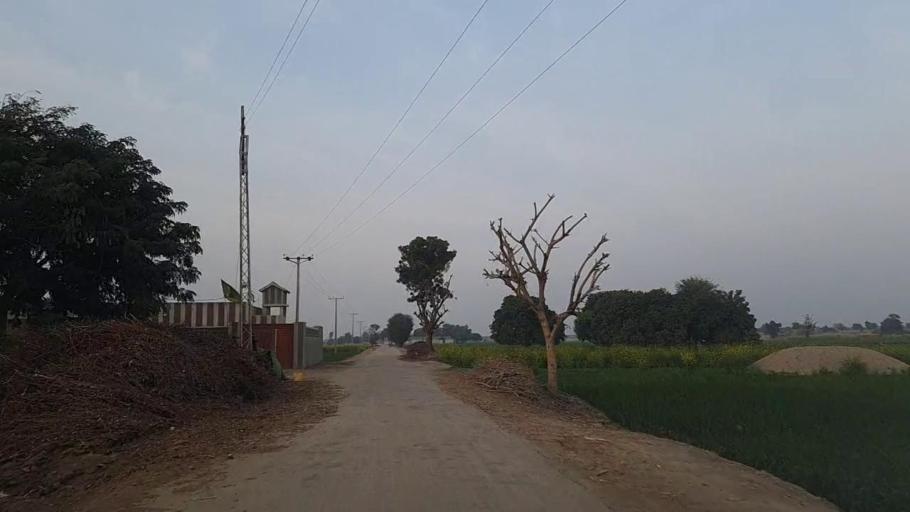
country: PK
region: Sindh
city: Jam Sahib
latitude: 26.4680
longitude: 68.5481
